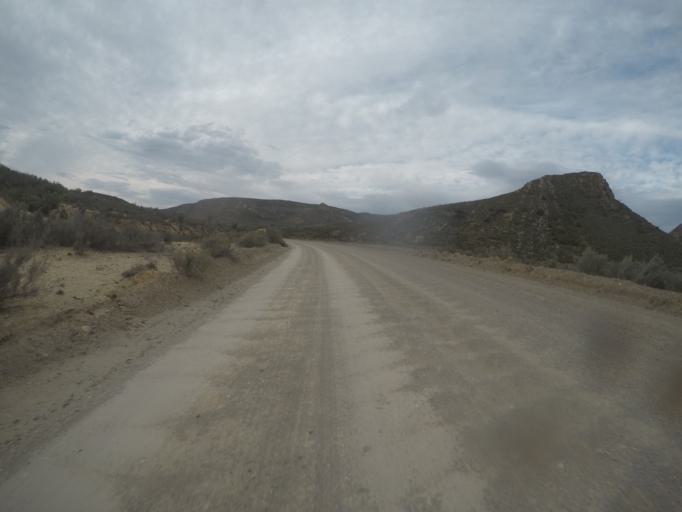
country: ZA
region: Eastern Cape
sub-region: Cacadu District Municipality
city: Willowmore
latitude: -33.5015
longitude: 23.6369
